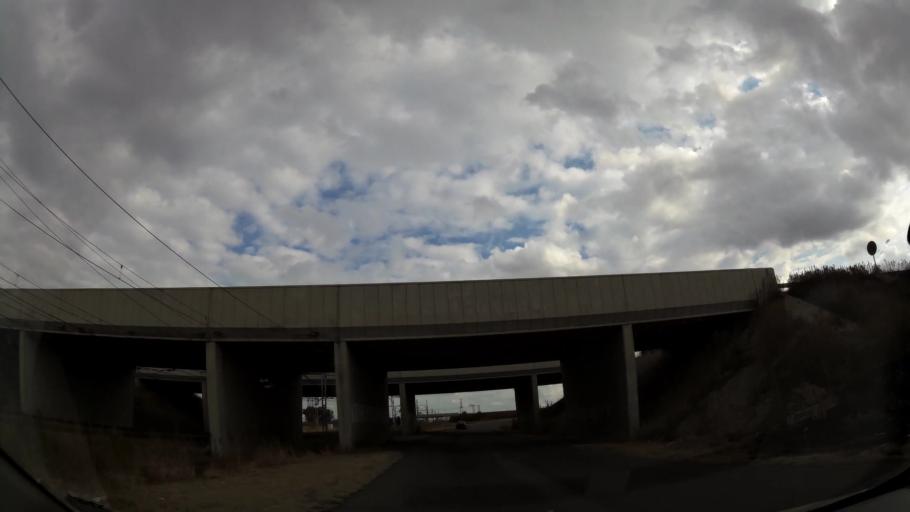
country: ZA
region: Orange Free State
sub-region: Fezile Dabi District Municipality
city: Sasolburg
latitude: -26.8388
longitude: 27.8754
